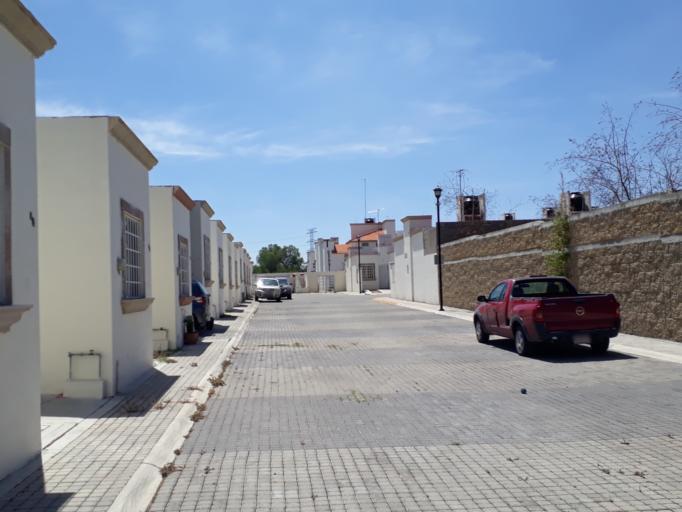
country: MX
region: Aguascalientes
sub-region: Aguascalientes
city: San Sebastian [Fraccionamiento]
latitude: 21.8105
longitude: -102.2973
